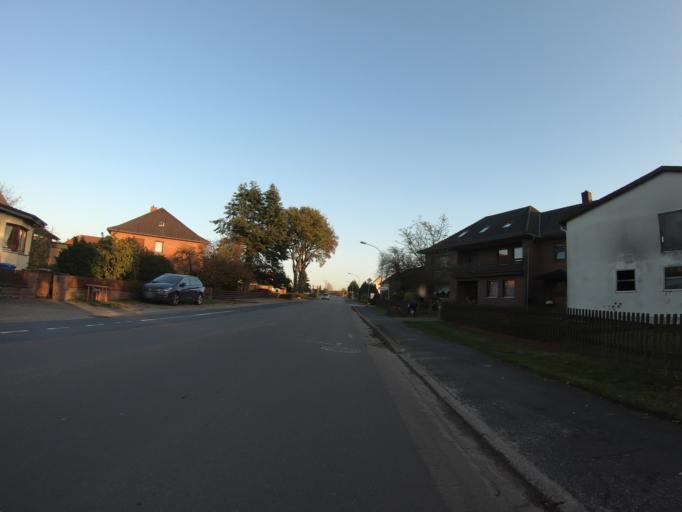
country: DE
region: Lower Saxony
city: Wagenhoff
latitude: 52.5081
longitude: 10.4835
